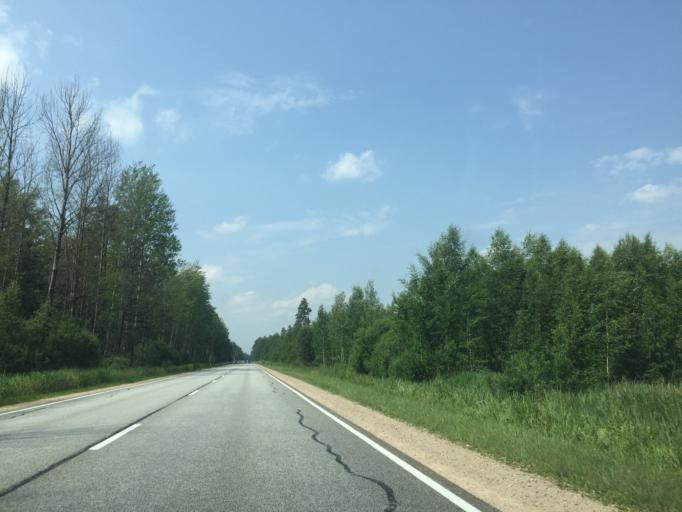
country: LV
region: Kekava
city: Balozi
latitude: 56.8178
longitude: 24.1154
